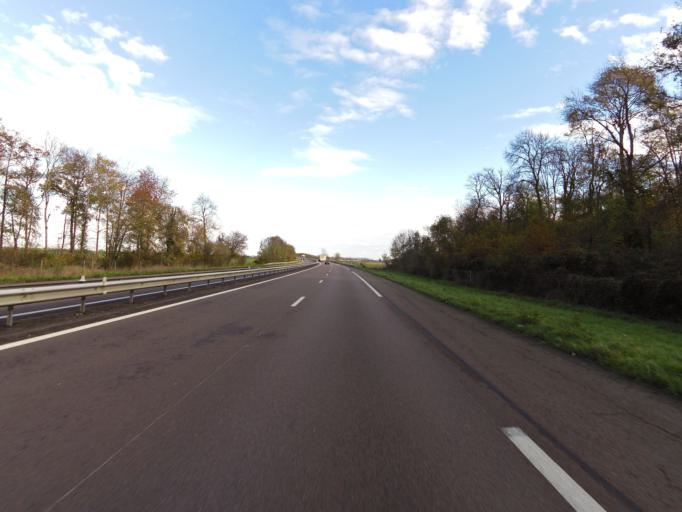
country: FR
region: Bourgogne
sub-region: Departement de la Cote-d'Or
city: Ouges
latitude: 47.2436
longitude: 5.0762
